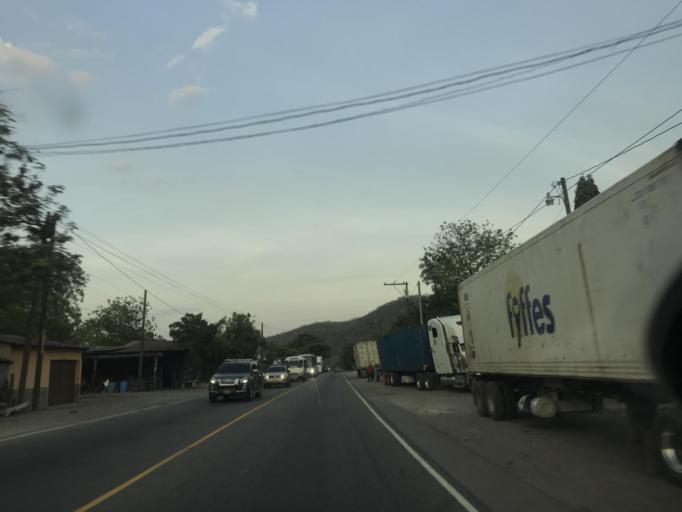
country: GT
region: Zacapa
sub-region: Municipio de Zacapa
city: Gualan
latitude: 15.0867
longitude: -89.4635
